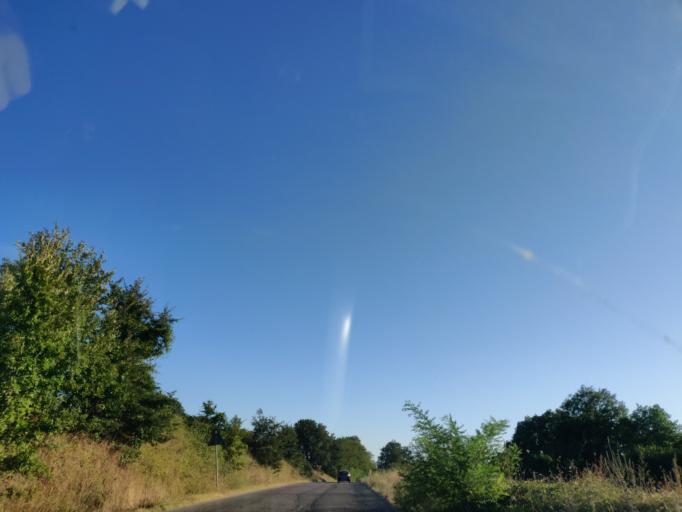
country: IT
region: Latium
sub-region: Provincia di Viterbo
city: Grotte di Castro
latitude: 42.7005
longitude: 11.8802
